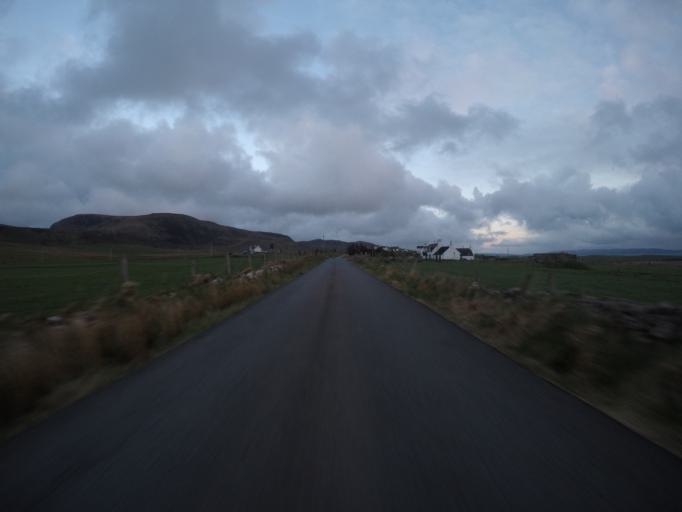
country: GB
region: Scotland
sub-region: Highland
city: Portree
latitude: 57.6438
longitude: -6.3778
